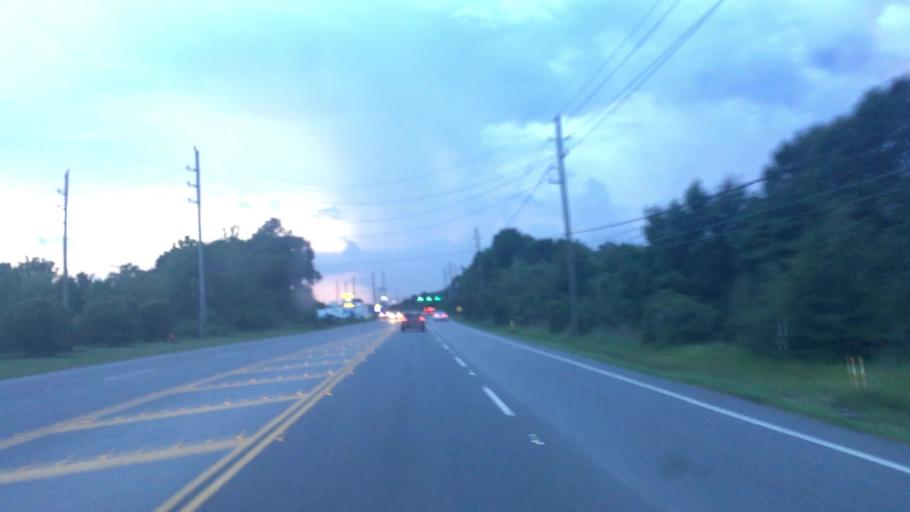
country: US
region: Texas
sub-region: Harris County
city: Humble
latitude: 29.9759
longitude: -95.2238
